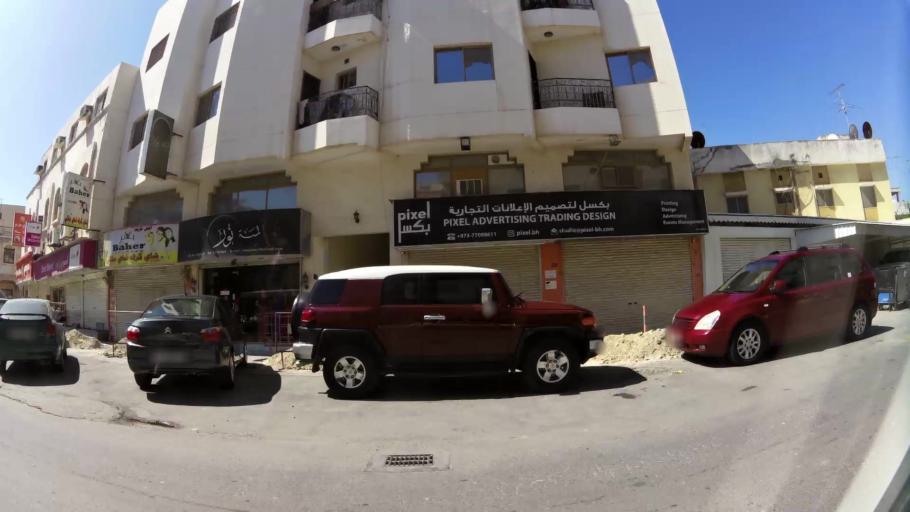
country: BH
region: Muharraq
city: Al Muharraq
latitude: 26.2622
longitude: 50.6175
